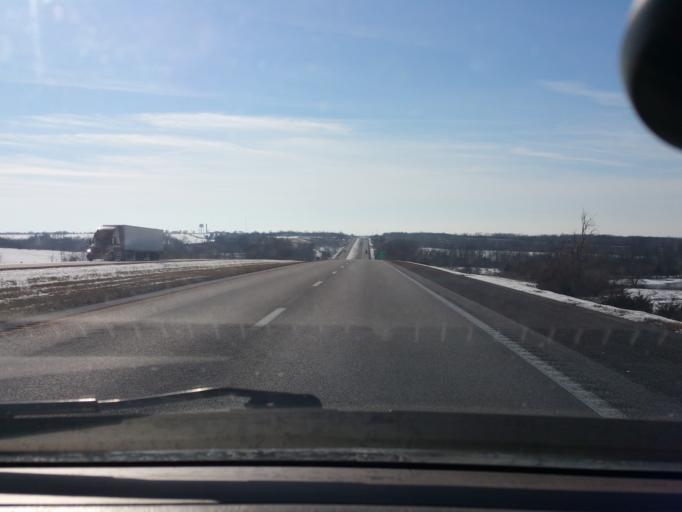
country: US
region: Missouri
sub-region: Daviess County
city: Gallatin
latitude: 39.9200
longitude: -94.1407
